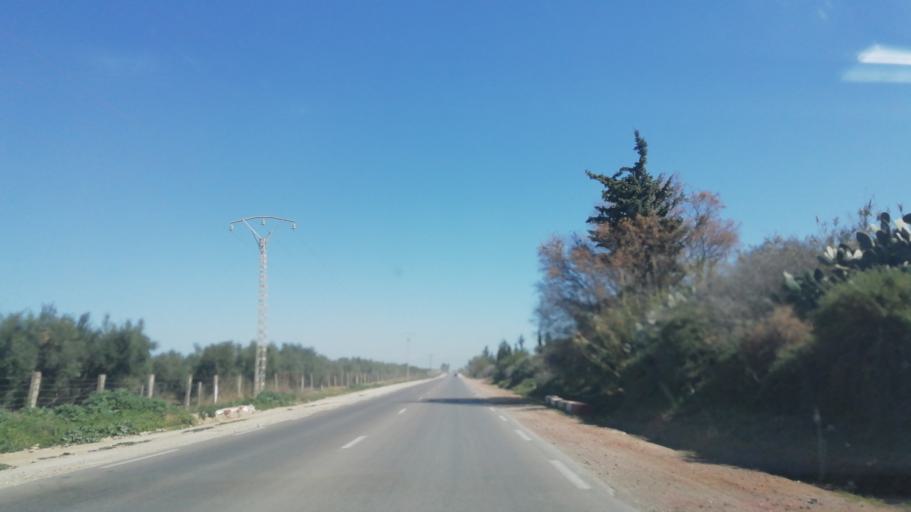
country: DZ
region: Mascara
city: Sig
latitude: 35.5364
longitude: -0.1381
